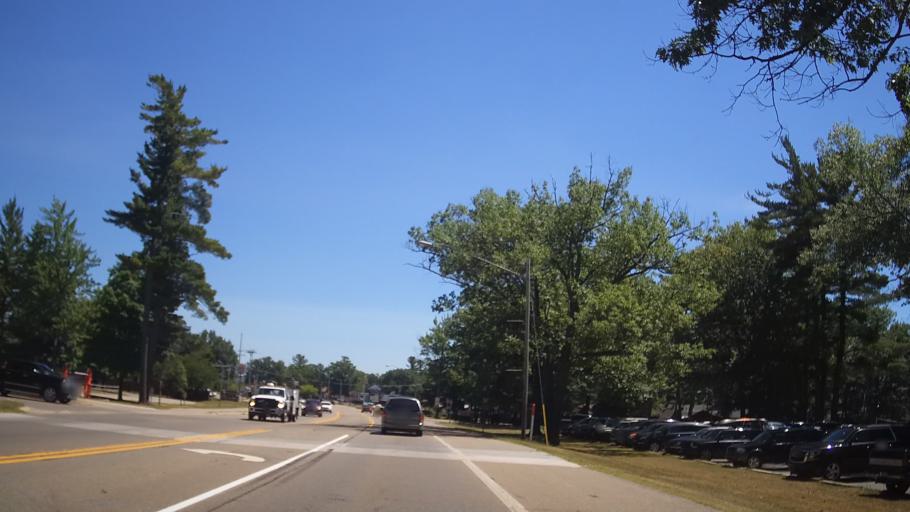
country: US
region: Michigan
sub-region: Wexford County
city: Cadillac
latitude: 44.2387
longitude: -85.4550
